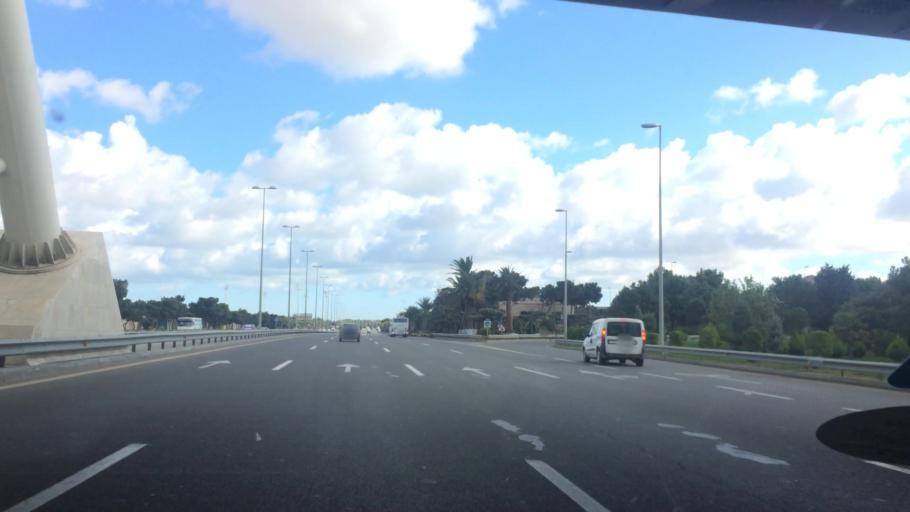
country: AZ
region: Baki
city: Biny Selo
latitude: 40.4593
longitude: 50.0759
